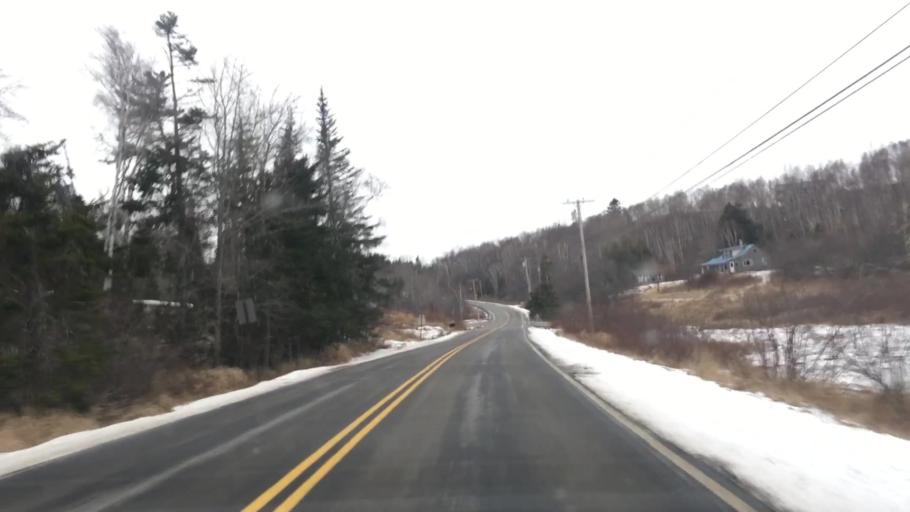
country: US
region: Maine
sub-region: Washington County
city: Machiasport
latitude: 44.7121
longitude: -67.3732
